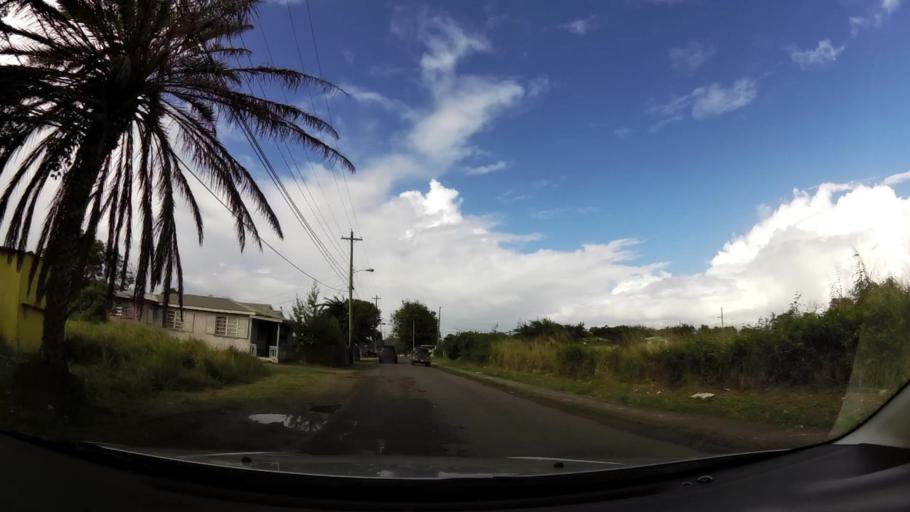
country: AG
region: Saint George
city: Piggotts
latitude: 17.1151
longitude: -61.8183
